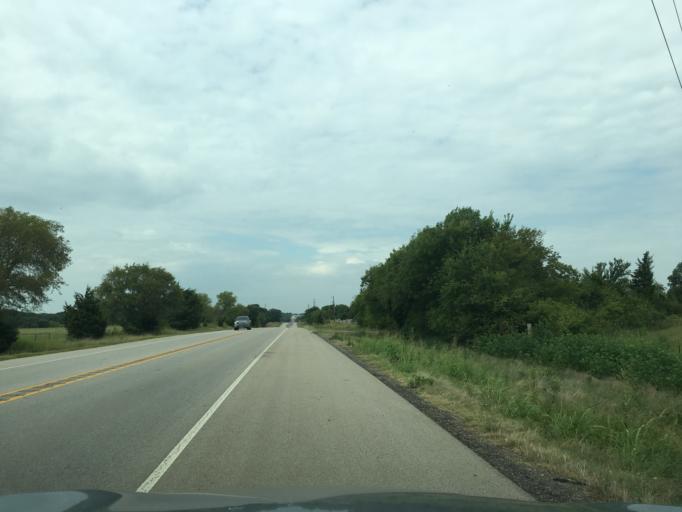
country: US
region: Texas
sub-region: Collin County
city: Anna
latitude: 33.3276
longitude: -96.4893
